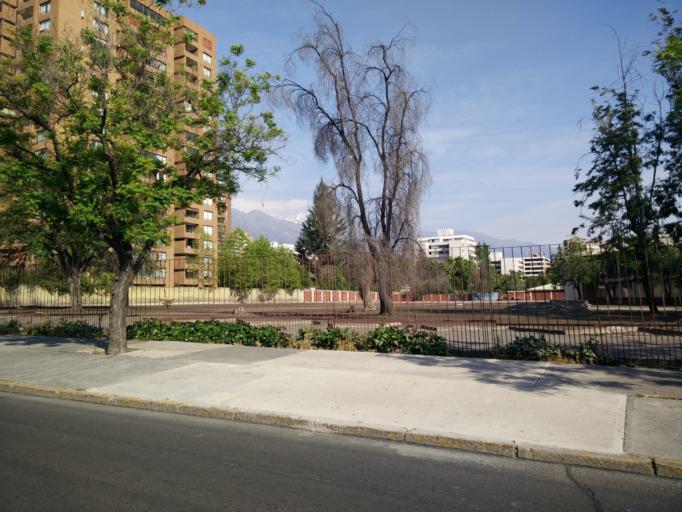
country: CL
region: Santiago Metropolitan
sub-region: Provincia de Santiago
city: Villa Presidente Frei, Nunoa, Santiago, Chile
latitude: -33.4179
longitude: -70.5758
